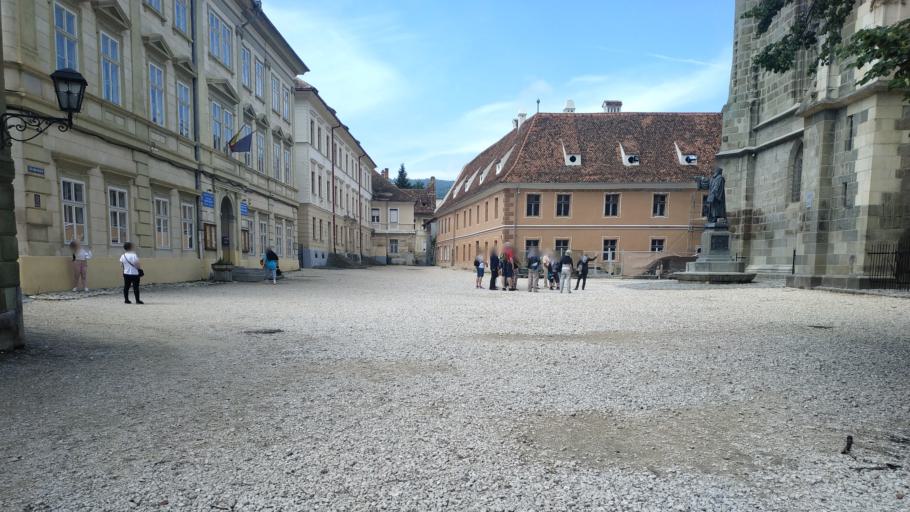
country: RO
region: Brasov
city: Brasov
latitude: 45.6408
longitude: 25.5882
